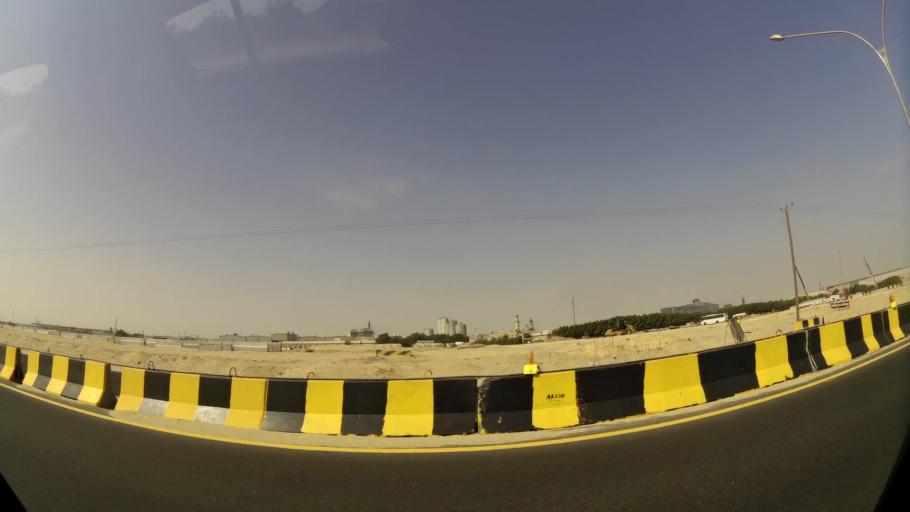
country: KW
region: Al Ahmadi
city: Al Fahahil
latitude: 28.9814
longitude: 48.1341
